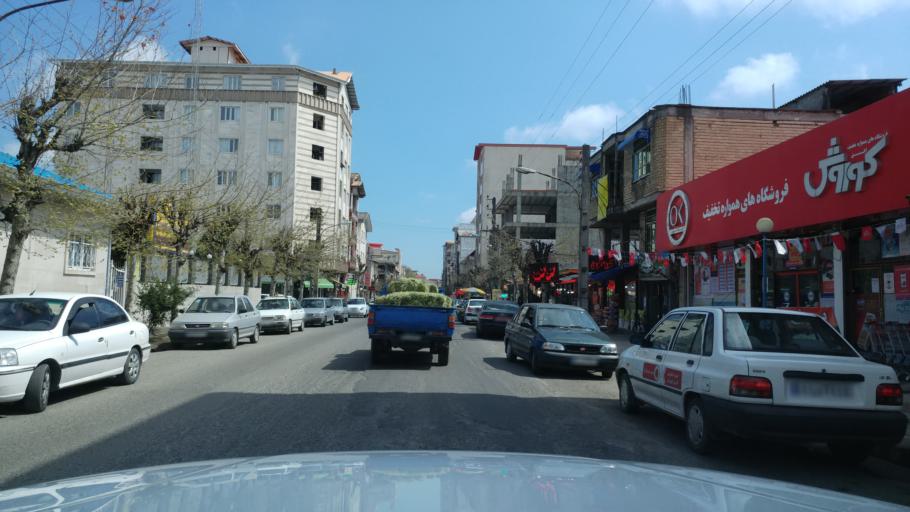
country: IR
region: Gilan
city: Hashtpar
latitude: 37.7930
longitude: 48.9074
